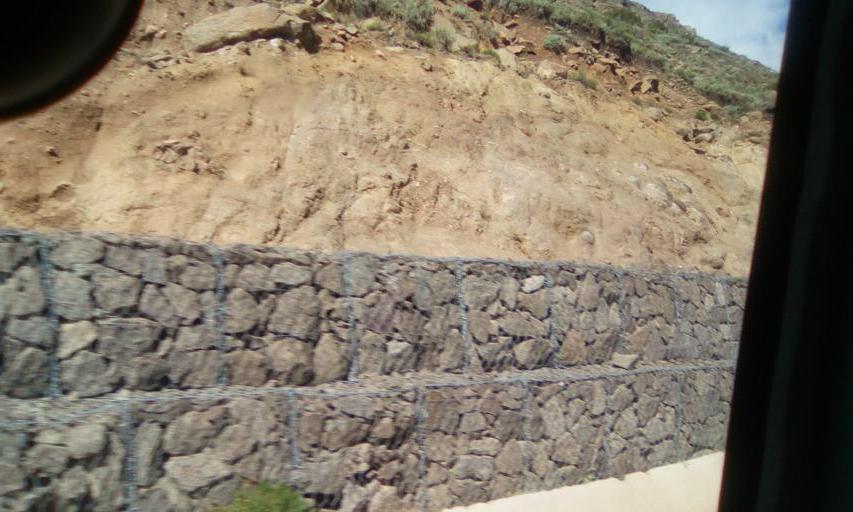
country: LS
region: Qacha's Nek
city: Qacha's Nek
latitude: -30.0050
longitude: 28.1597
